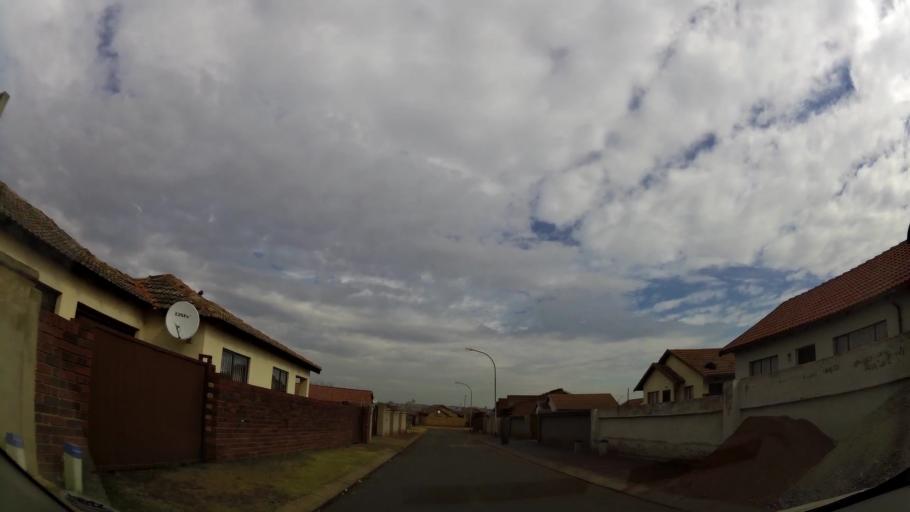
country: ZA
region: Gauteng
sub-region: Ekurhuleni Metropolitan Municipality
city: Germiston
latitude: -26.3160
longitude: 28.1754
